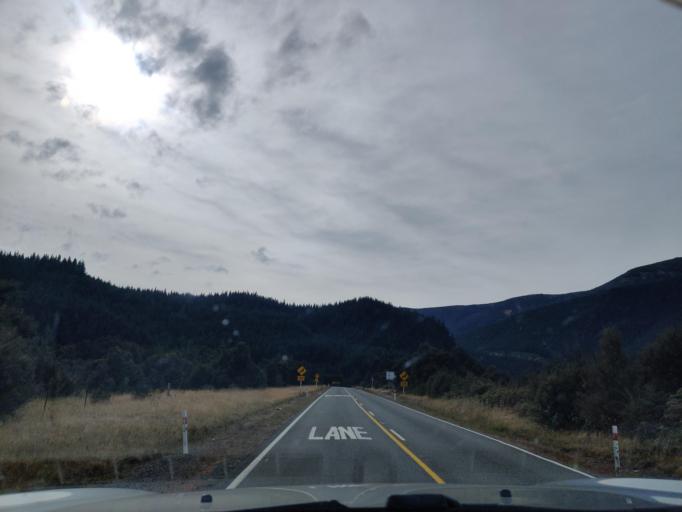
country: NZ
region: Tasman
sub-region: Tasman District
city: Wakefield
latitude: -41.7142
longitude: 173.0883
